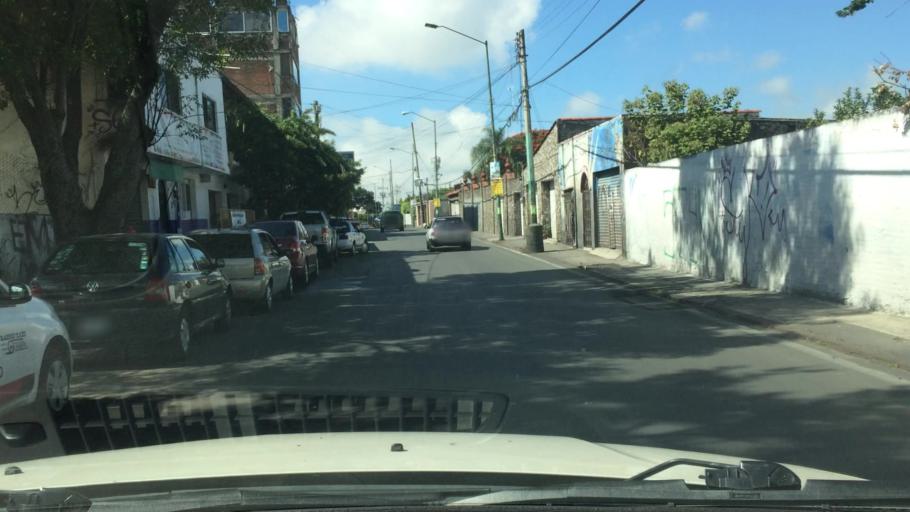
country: MX
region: Morelos
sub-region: Cuernavaca
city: Cuernavaca
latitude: 18.9312
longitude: -99.2401
